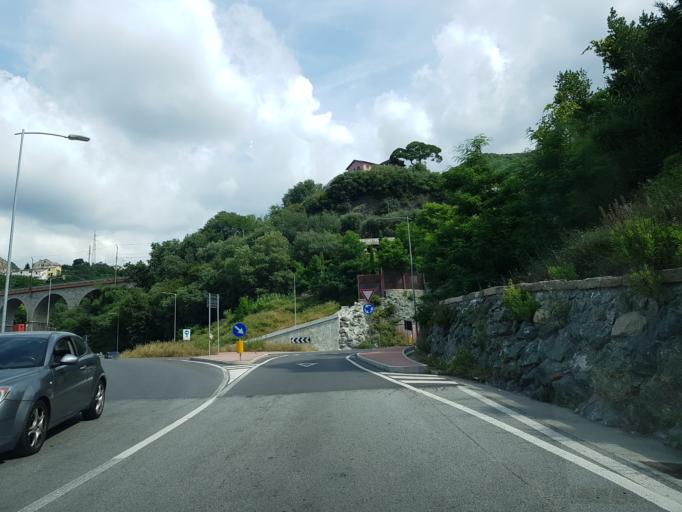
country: IT
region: Liguria
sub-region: Provincia di Genova
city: San Teodoro
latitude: 44.4333
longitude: 8.8613
